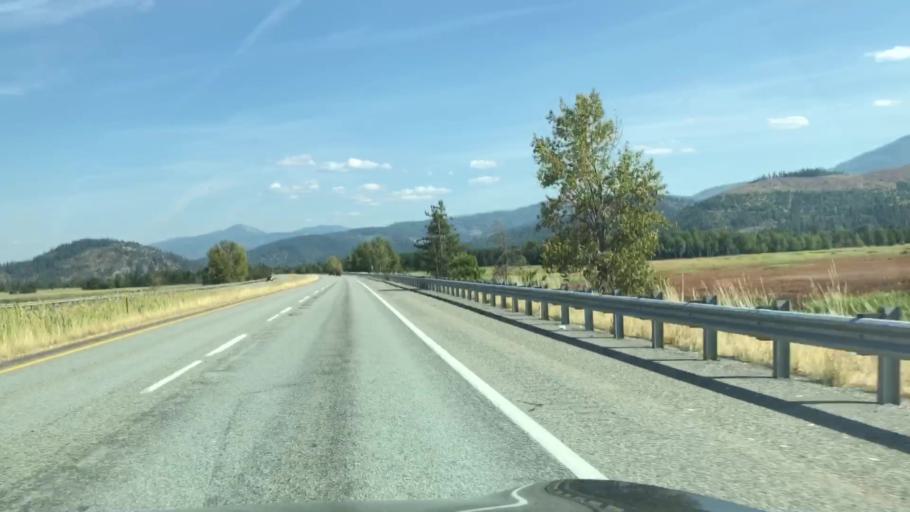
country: US
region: Idaho
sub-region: Shoshone County
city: Pinehurst
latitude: 47.5605
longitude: -116.3954
